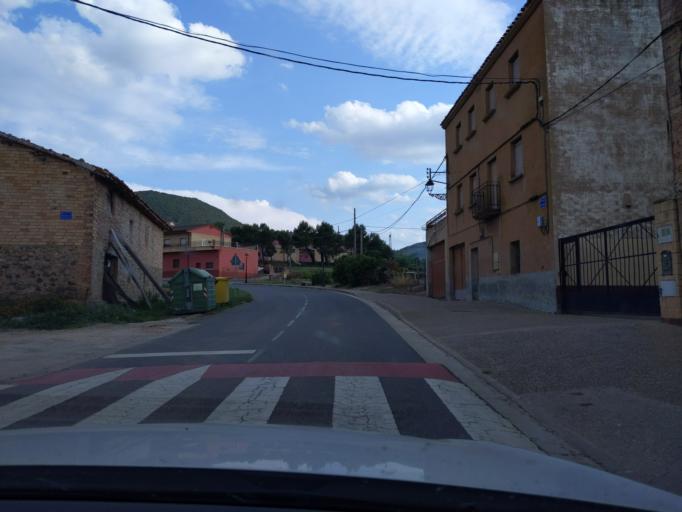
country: ES
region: La Rioja
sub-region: Provincia de La Rioja
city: Clavijo
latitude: 42.3703
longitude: -2.4230
